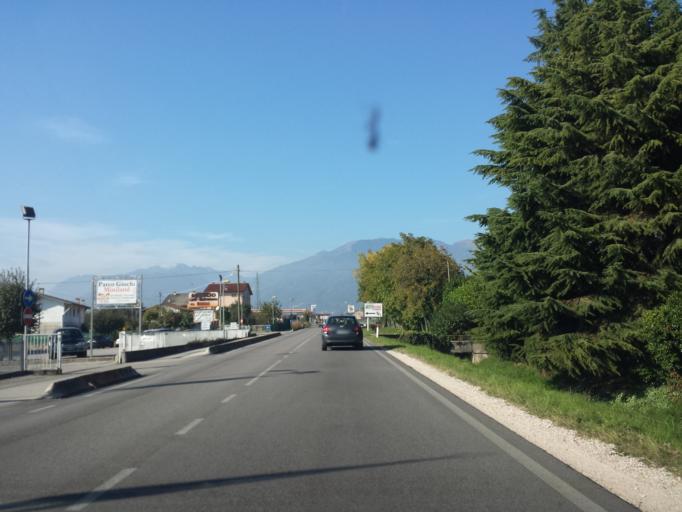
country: IT
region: Veneto
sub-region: Provincia di Vicenza
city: San Vito di Leguzzano
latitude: 45.6926
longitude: 11.3902
